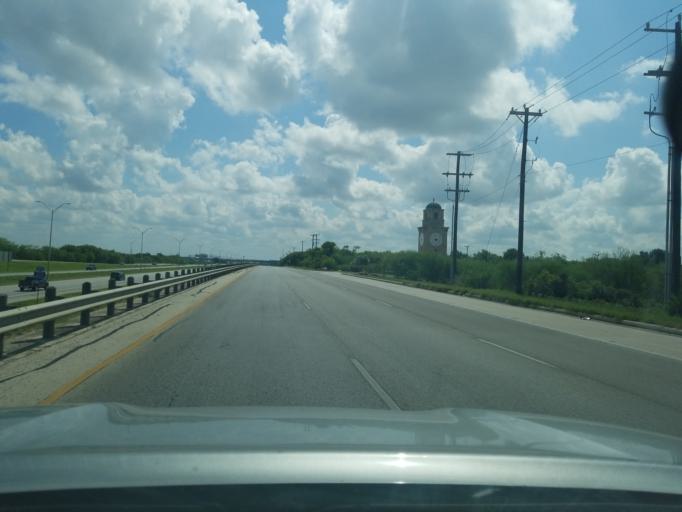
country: US
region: Texas
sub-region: Bexar County
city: San Antonio
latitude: 29.3197
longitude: -98.5259
